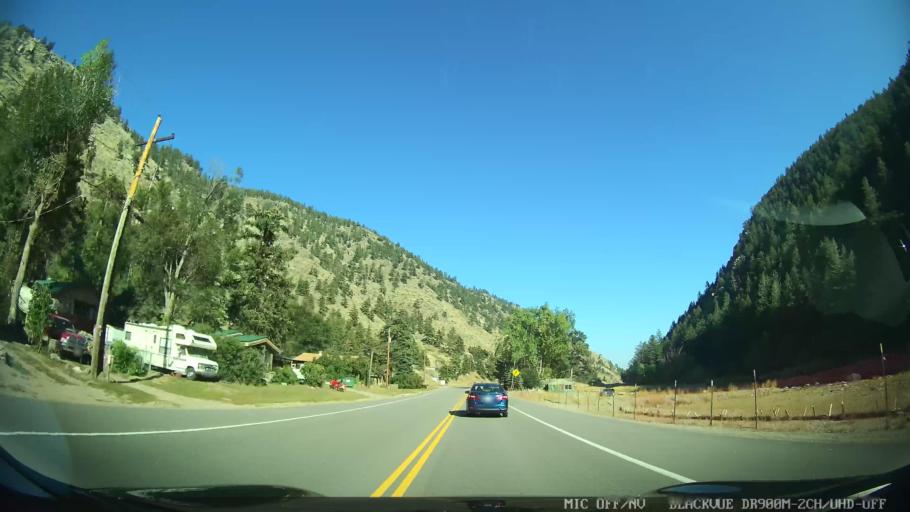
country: US
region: Colorado
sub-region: Larimer County
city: Estes Park
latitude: 40.4323
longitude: -105.3382
